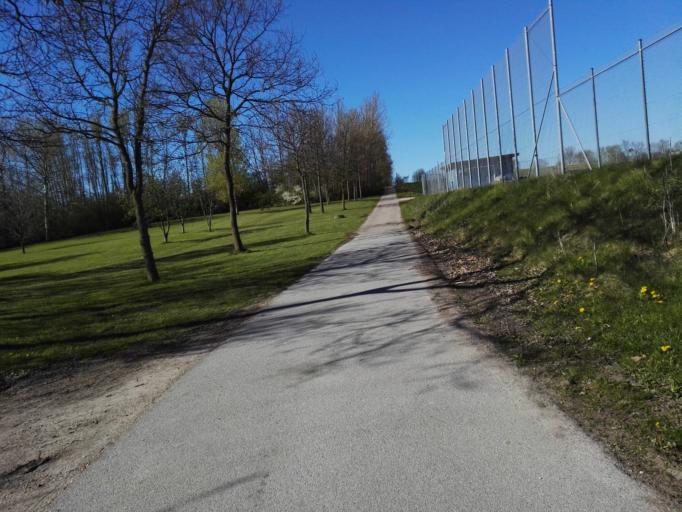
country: DK
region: Capital Region
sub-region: Egedal Kommune
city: Stenlose
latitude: 55.7571
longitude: 12.2020
